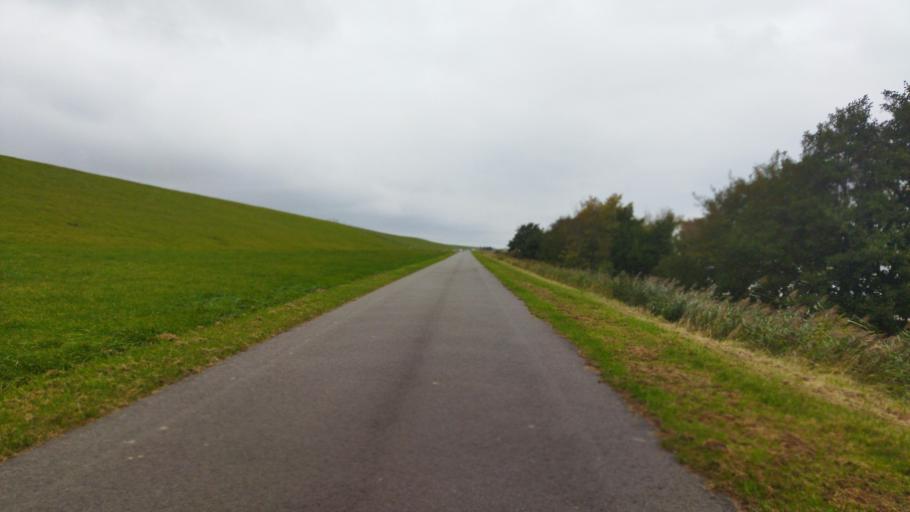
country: NL
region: Groningen
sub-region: Gemeente Delfzijl
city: Delfzijl
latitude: 53.4217
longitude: 7.0142
